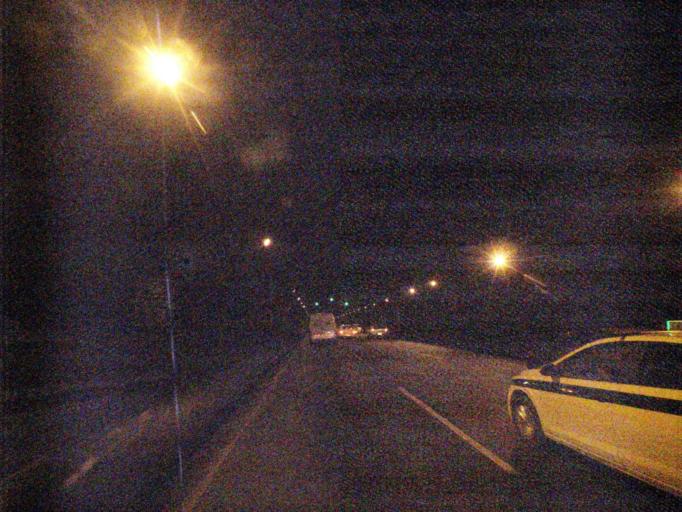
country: BR
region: Rio de Janeiro
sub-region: Rio De Janeiro
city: Rio de Janeiro
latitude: -22.9459
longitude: -43.2027
